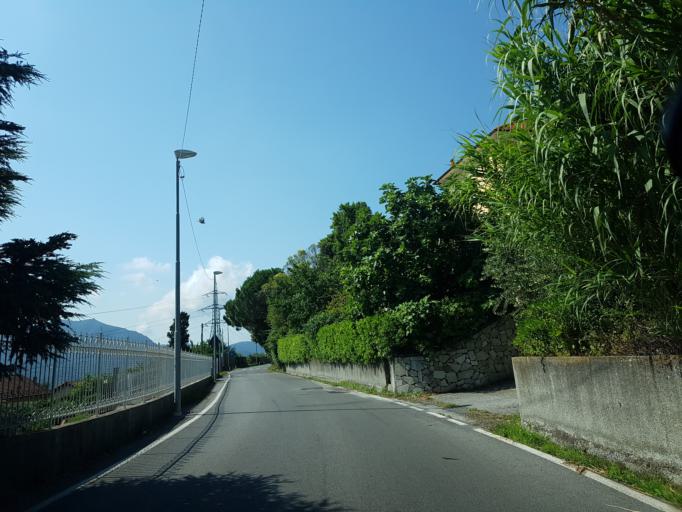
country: IT
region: Liguria
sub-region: Provincia di Genova
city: Pedemonte
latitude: 44.4918
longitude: 8.9129
